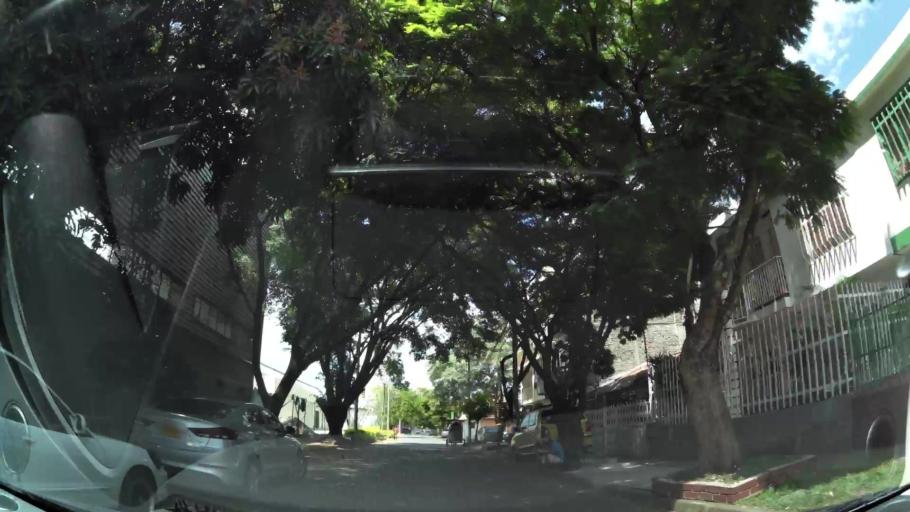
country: CO
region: Valle del Cauca
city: Cali
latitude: 3.3842
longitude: -76.5237
